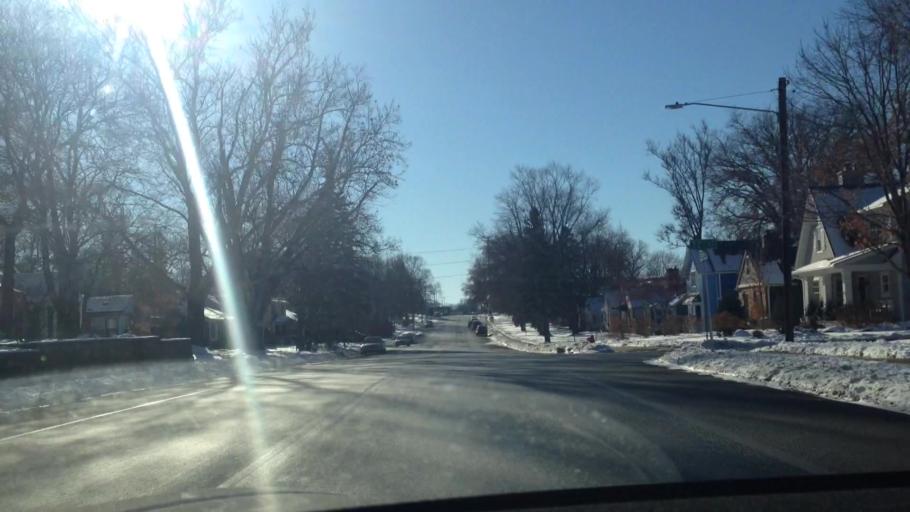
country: US
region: Minnesota
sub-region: Hennepin County
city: Saint Louis Park
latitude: 44.9463
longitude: -93.3605
